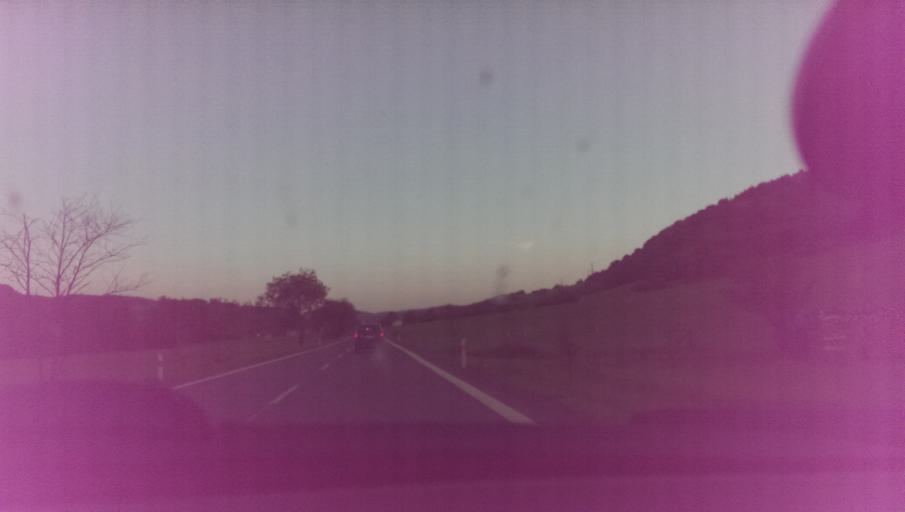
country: CZ
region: Zlin
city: Valasska Polanka
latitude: 49.2977
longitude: 18.0013
